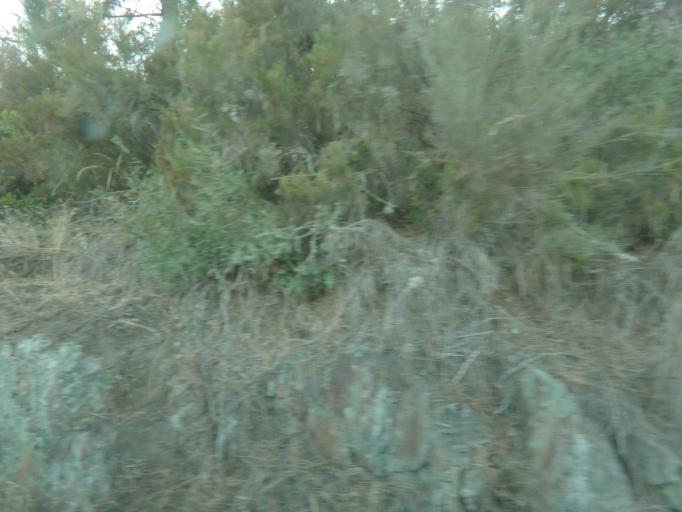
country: PT
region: Vila Real
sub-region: Sabrosa
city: Vilela
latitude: 41.1728
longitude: -7.5902
